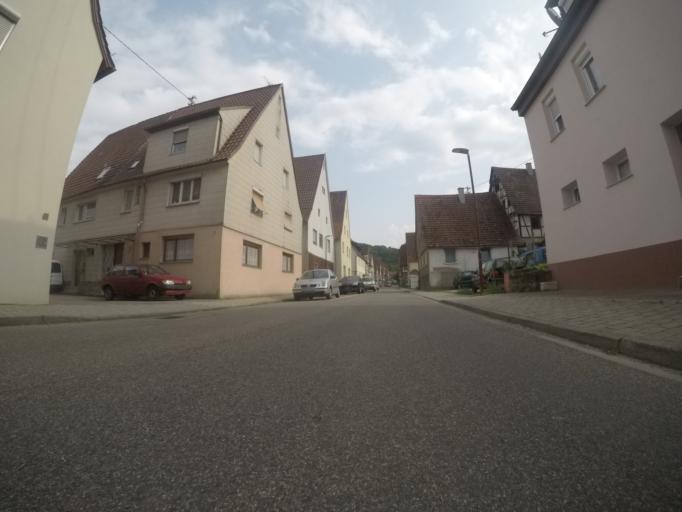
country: DE
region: Baden-Wuerttemberg
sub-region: Regierungsbezirk Stuttgart
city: Eberdingen
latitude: 48.8805
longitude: 8.9644
